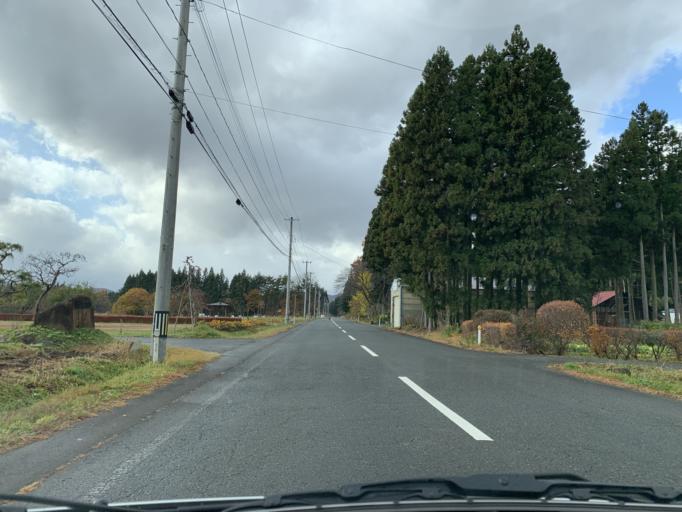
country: JP
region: Iwate
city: Mizusawa
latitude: 39.1111
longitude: 140.9849
